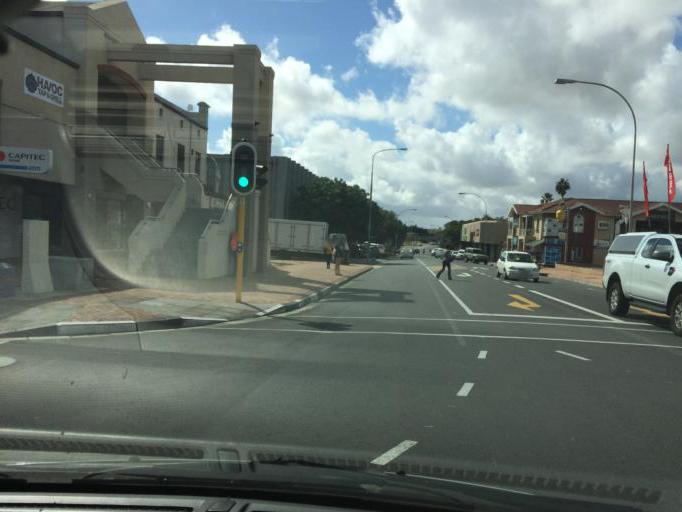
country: ZA
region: Western Cape
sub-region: City of Cape Town
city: Kraaifontein
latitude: -33.8297
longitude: 18.6497
